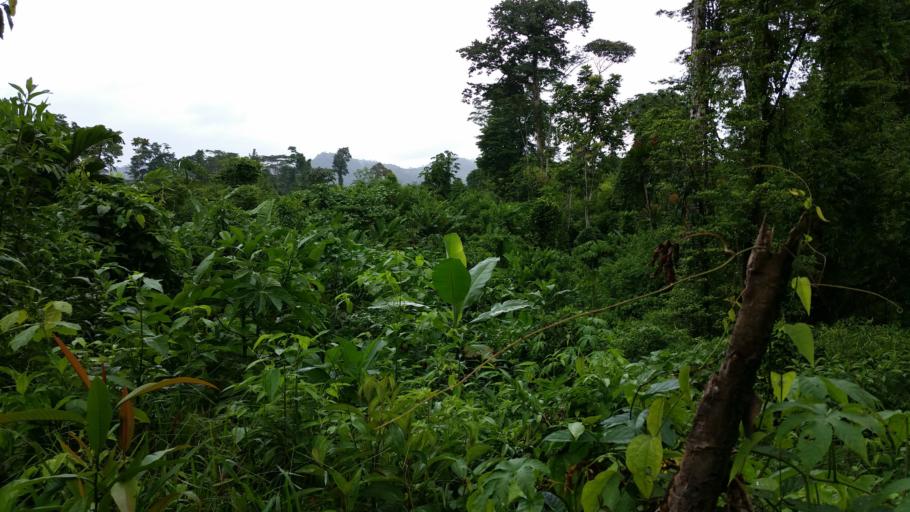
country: NI
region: Atlantico Norte (RAAN)
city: Bonanza
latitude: 14.0940
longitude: -84.6764
